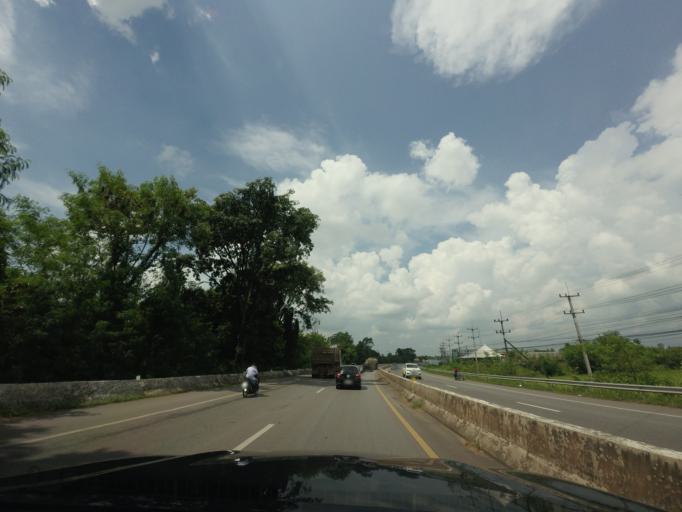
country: TH
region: Khon Kaen
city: Nong Ruea
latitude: 16.4881
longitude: 102.4176
